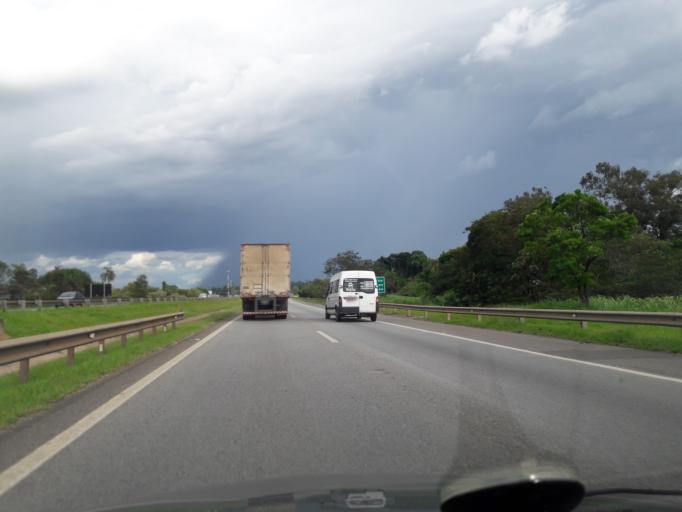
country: BR
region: Sao Paulo
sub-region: Atibaia
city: Atibaia
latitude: -23.1005
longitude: -46.5369
